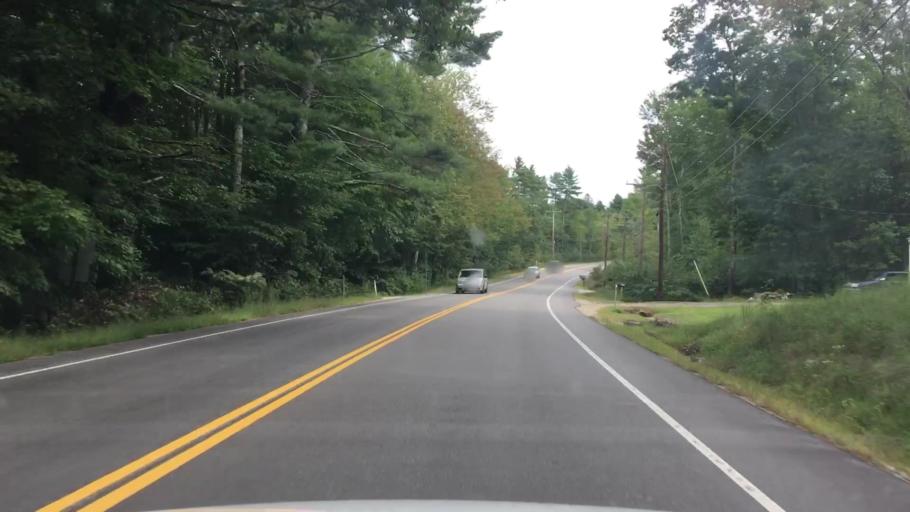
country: US
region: New Hampshire
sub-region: Strafford County
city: Madbury
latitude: 43.2056
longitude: -70.9717
